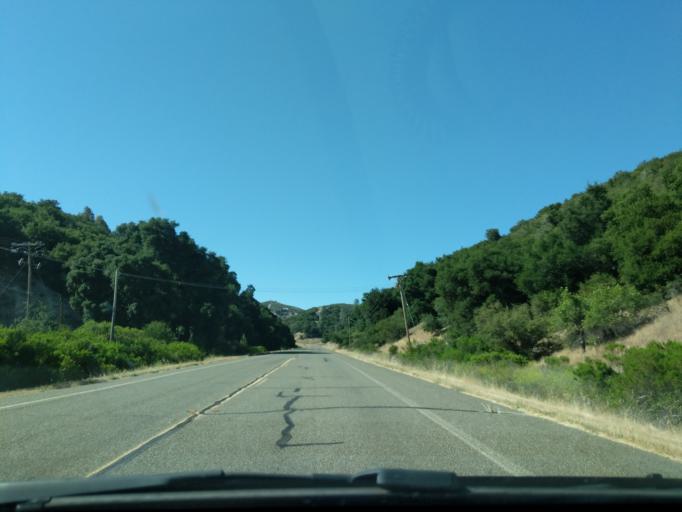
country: US
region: California
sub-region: Monterey County
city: King City
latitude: 36.0641
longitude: -121.1846
